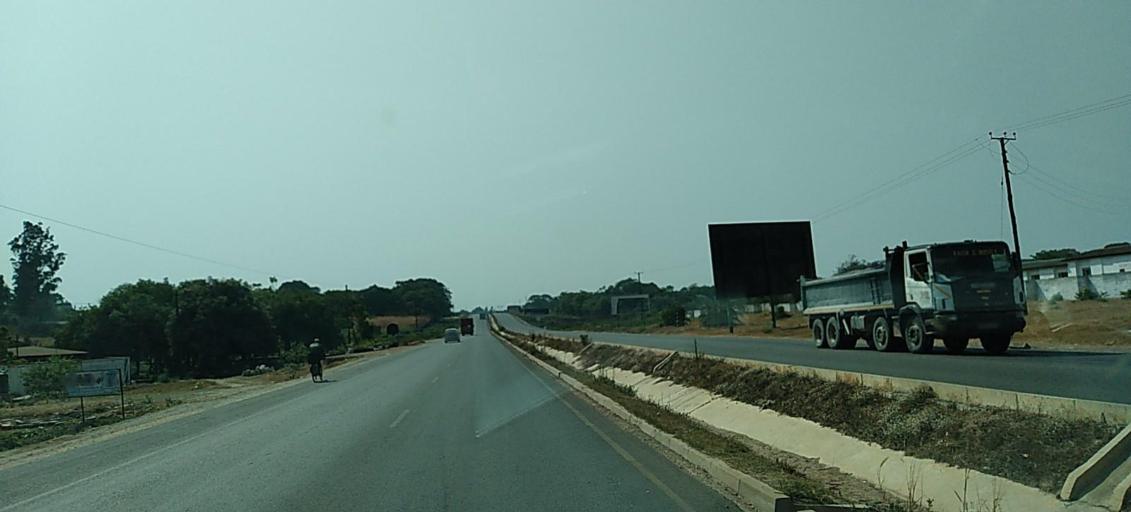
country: ZM
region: Copperbelt
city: Chingola
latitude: -12.5581
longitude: 27.8756
